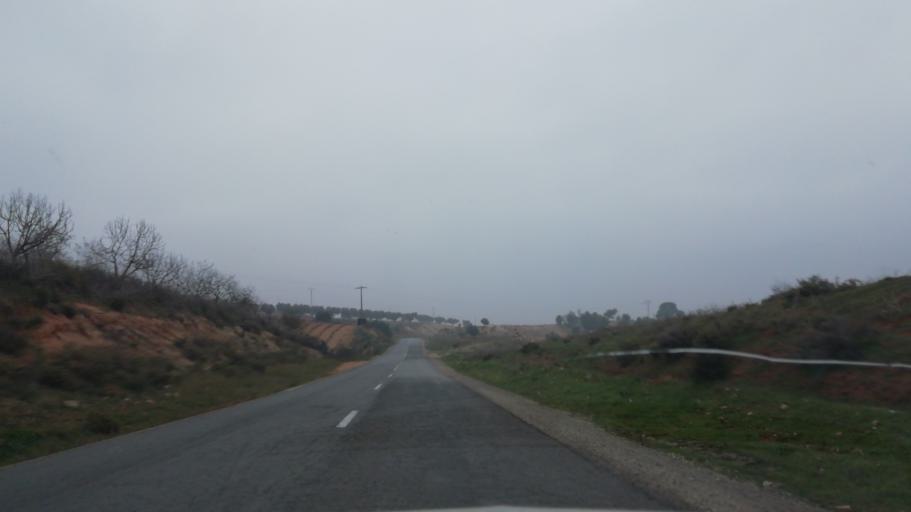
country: DZ
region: Mascara
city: Mascara
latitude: 35.4133
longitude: 0.1543
